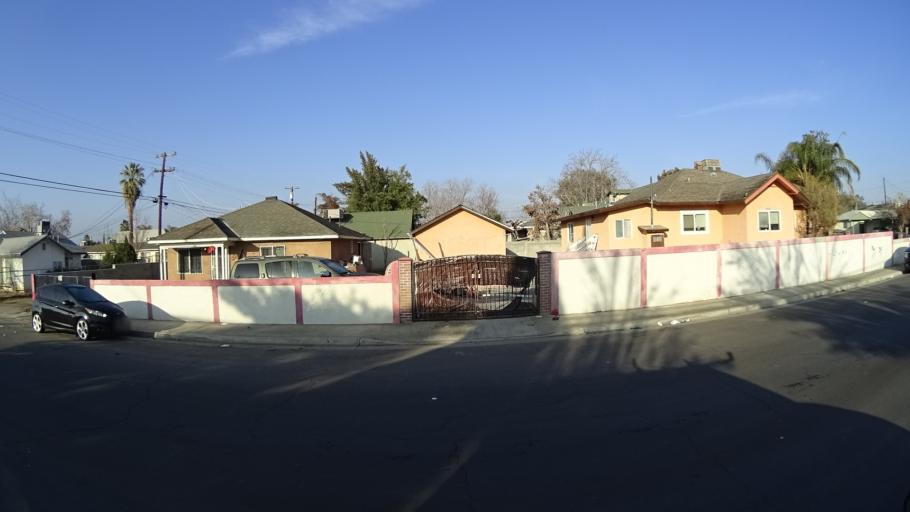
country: US
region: California
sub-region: Kern County
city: Bakersfield
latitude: 35.3823
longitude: -118.9842
